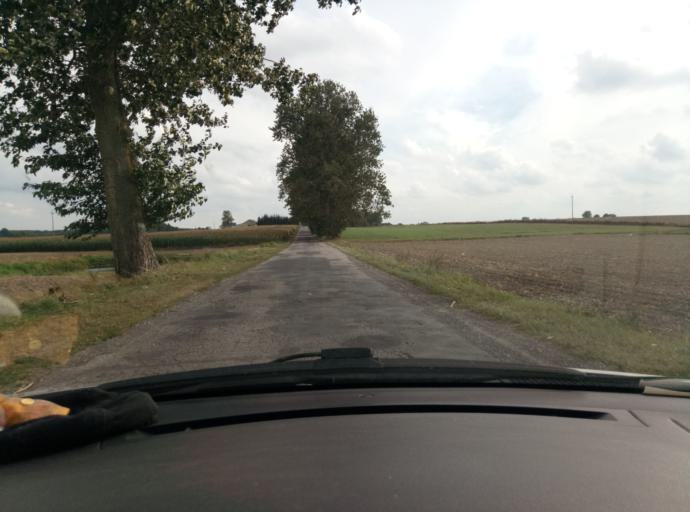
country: PL
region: Kujawsko-Pomorskie
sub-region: Powiat brodnicki
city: Jablonowo Pomorskie
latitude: 53.3833
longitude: 19.2455
